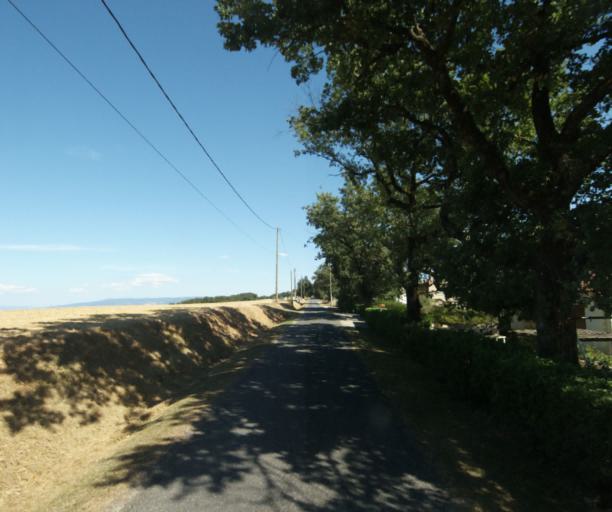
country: FR
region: Midi-Pyrenees
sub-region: Departement de la Haute-Garonne
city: Saint-Felix-Lauragais
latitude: 43.5196
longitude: 1.9155
